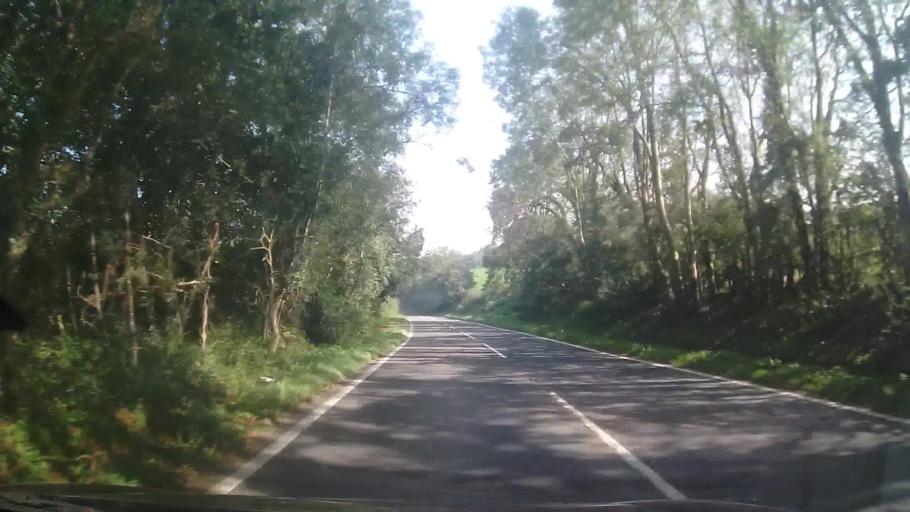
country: GB
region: Wales
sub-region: Pembrokeshire
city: Nevern
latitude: 52.0168
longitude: -4.7891
